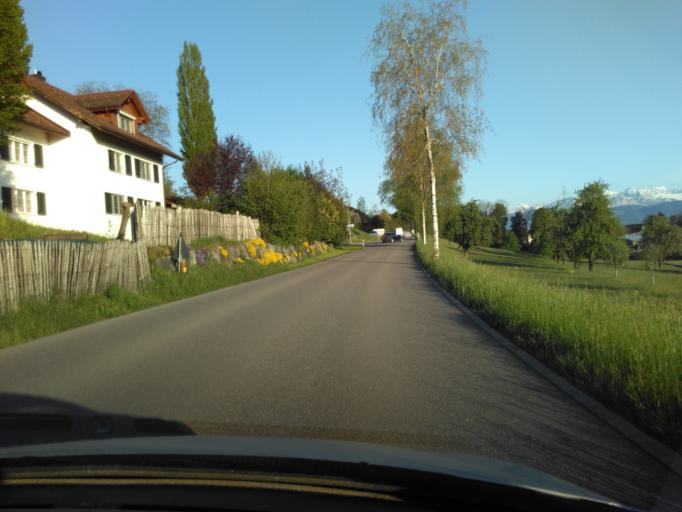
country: CH
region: Zurich
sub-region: Bezirk Hinwil
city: Hadlikon
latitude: 47.2775
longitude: 8.8616
